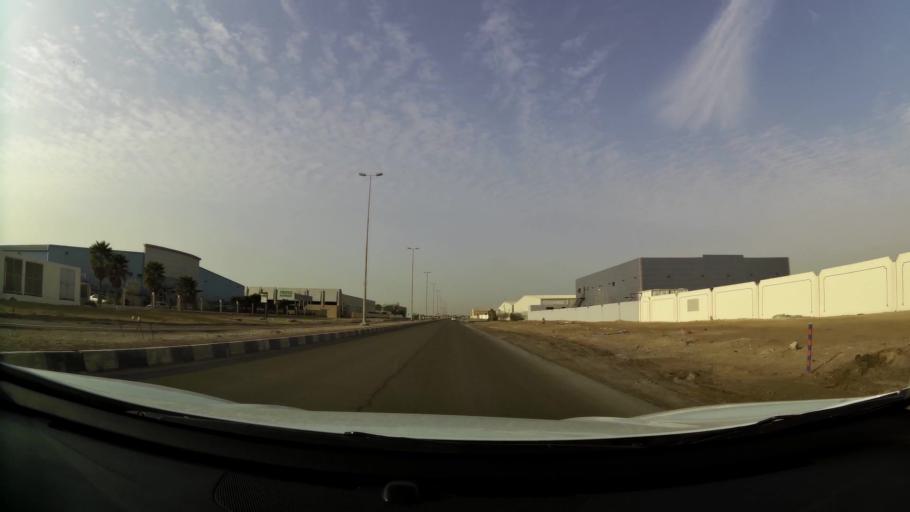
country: AE
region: Abu Dhabi
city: Abu Dhabi
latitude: 24.3307
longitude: 54.5167
